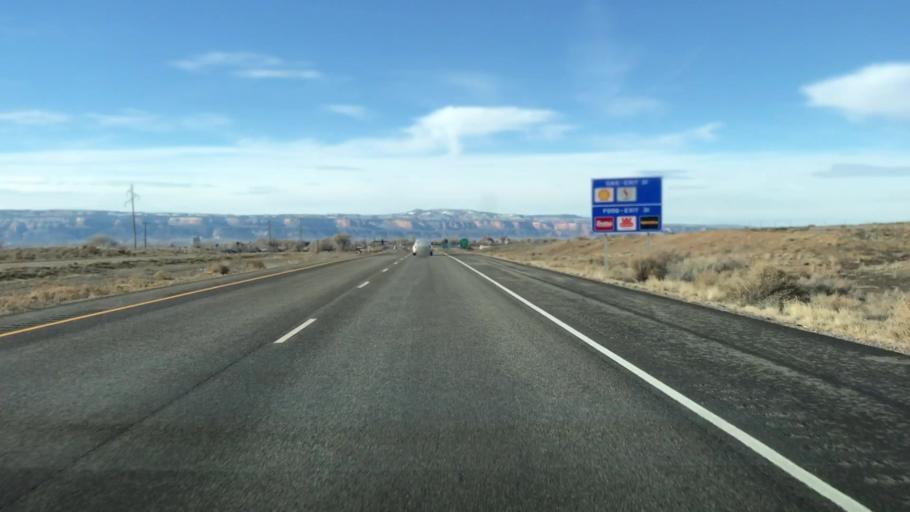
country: US
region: Colorado
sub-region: Mesa County
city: Fruitvale
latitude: 39.1068
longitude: -108.5198
